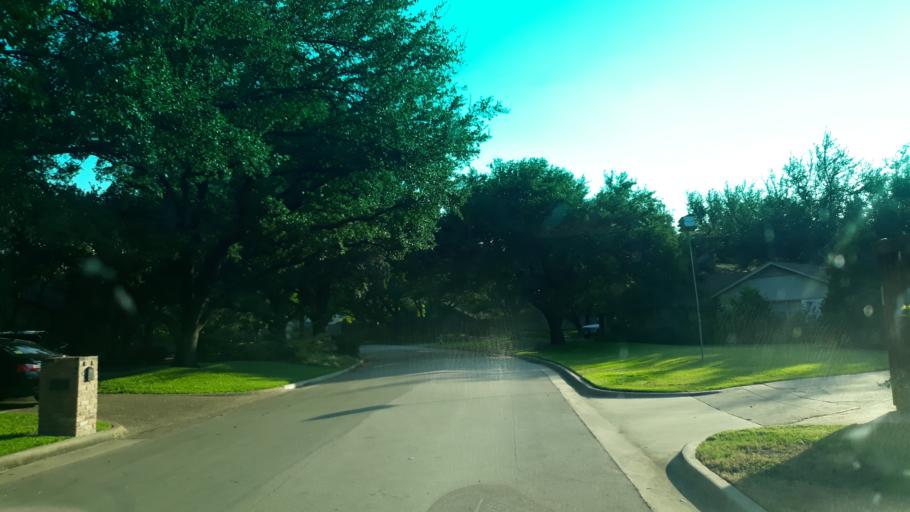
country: US
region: Texas
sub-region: Dallas County
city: Addison
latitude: 32.9441
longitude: -96.7936
